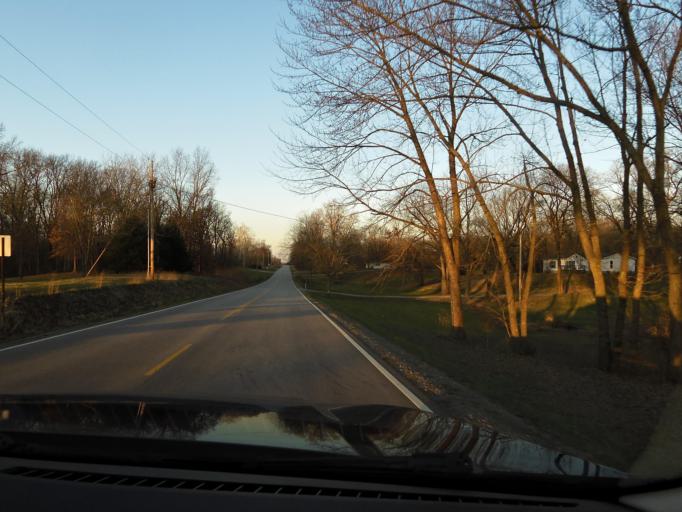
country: US
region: Illinois
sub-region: Marion County
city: Salem
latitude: 38.7586
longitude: -88.9265
